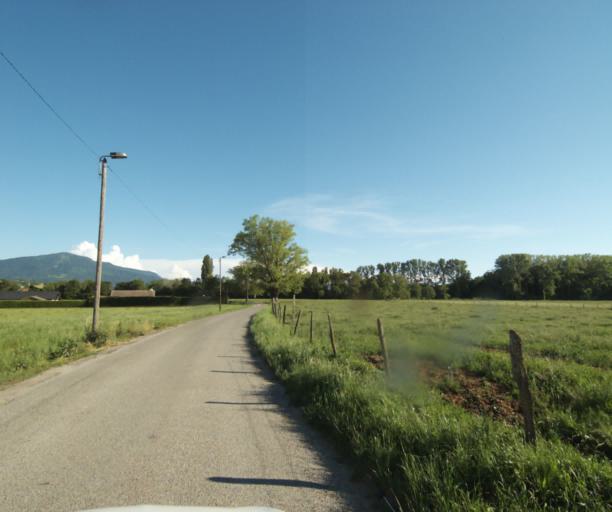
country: FR
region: Rhone-Alpes
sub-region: Departement de la Haute-Savoie
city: Douvaine
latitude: 46.3014
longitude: 6.3022
